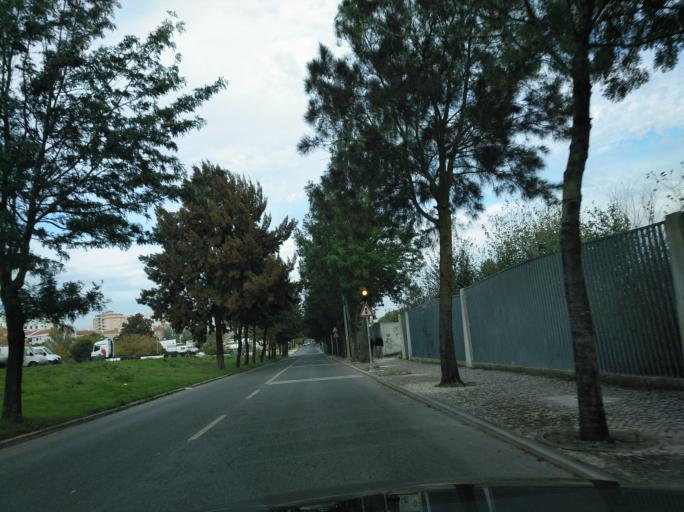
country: PT
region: Lisbon
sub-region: Sintra
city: Queluz
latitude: 38.7537
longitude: -9.2541
